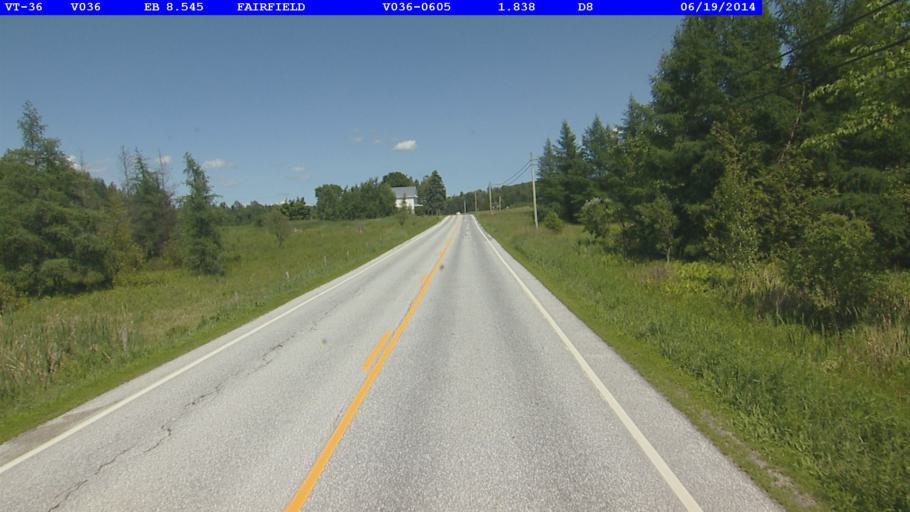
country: US
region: Vermont
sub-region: Franklin County
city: Saint Albans
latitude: 44.7881
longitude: -72.9949
